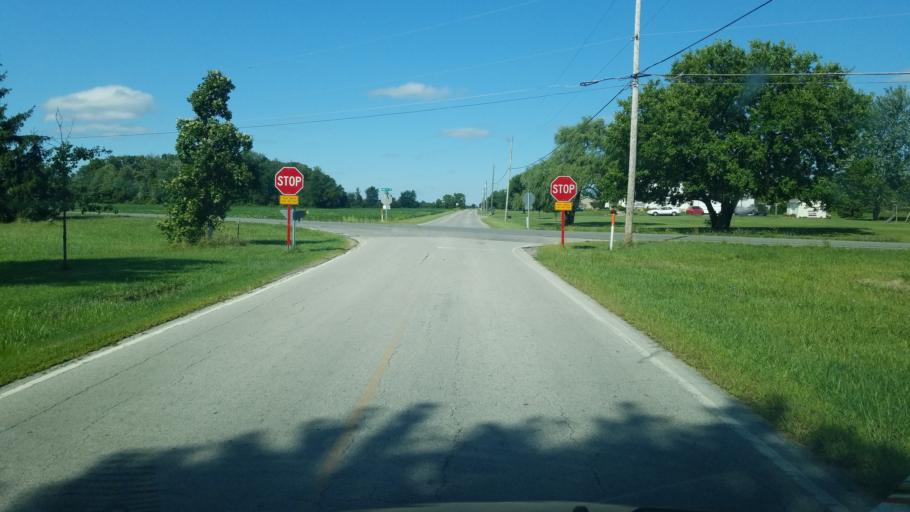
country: US
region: Ohio
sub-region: Hancock County
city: Findlay
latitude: 41.1092
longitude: -83.5959
